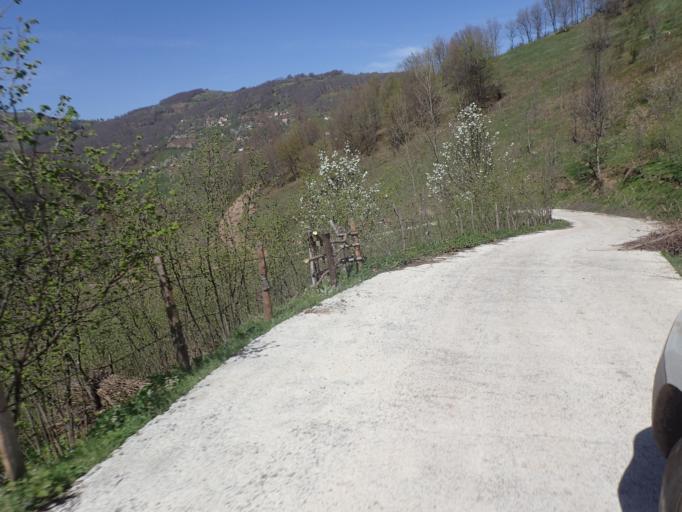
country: TR
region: Ordu
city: Aybasti
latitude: 40.7086
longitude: 37.2726
